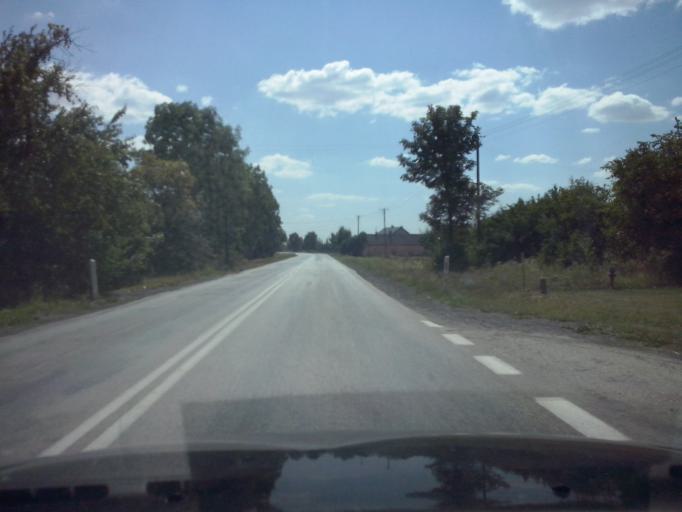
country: PL
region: Swietokrzyskie
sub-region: Powiat staszowski
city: Szydlow
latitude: 50.6122
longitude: 21.0092
